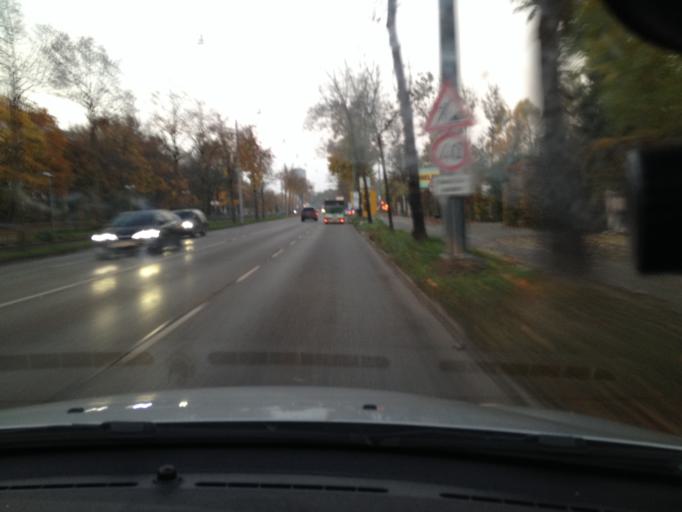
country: DE
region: Bavaria
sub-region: Swabia
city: Augsburg
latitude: 48.3348
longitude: 10.9078
